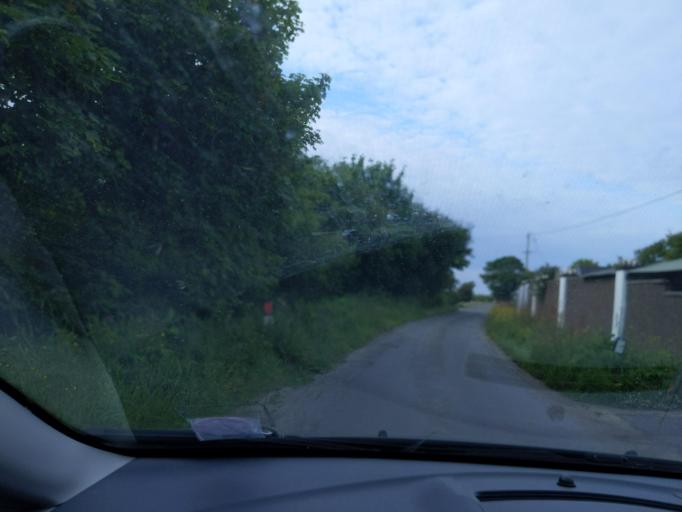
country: IM
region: Ramsey
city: Ramsey
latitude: 54.3901
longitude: -4.4477
